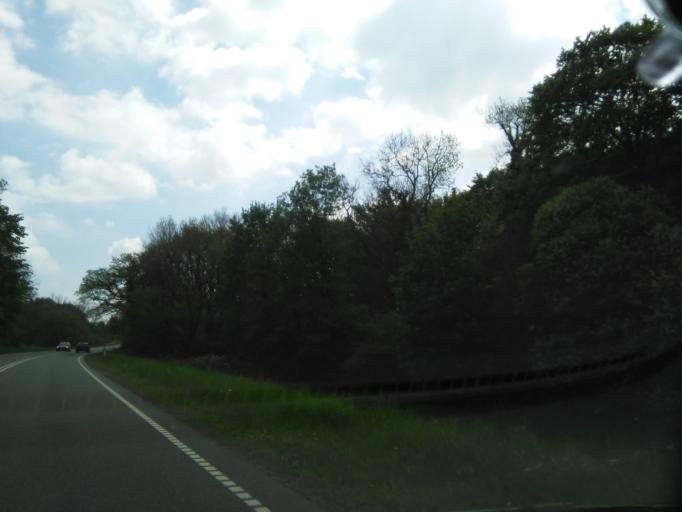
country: DK
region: Central Jutland
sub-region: Skanderborg Kommune
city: Stilling
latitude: 56.0074
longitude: 9.9962
